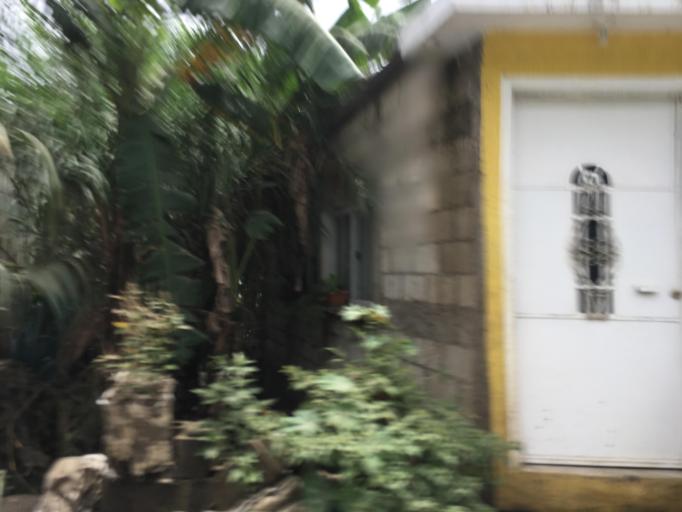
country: GT
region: Guatemala
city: Villa Canales
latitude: 14.4548
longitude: -90.5717
